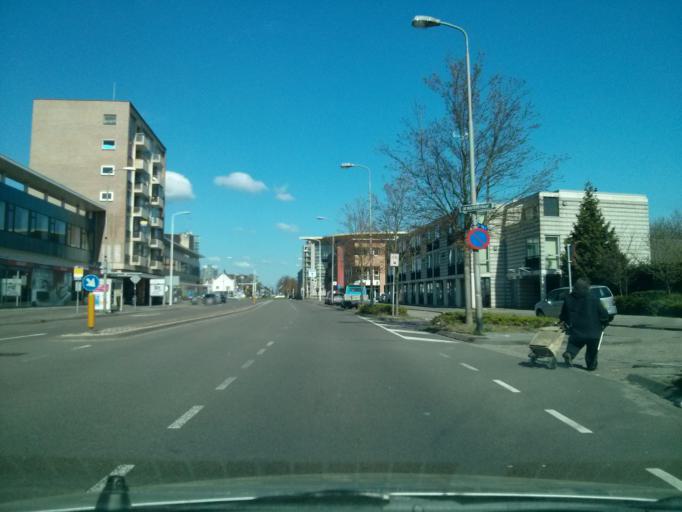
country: NL
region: North Brabant
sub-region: Gemeente Eindhoven
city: Eindhoven
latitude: 51.4503
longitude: 5.4662
